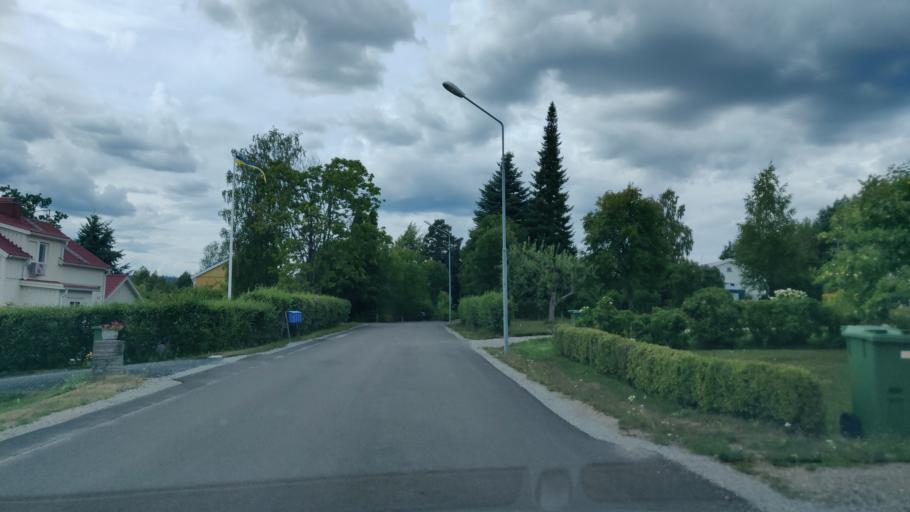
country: SE
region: Vaermland
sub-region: Hagfors Kommun
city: Hagfors
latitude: 60.0424
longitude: 13.6740
